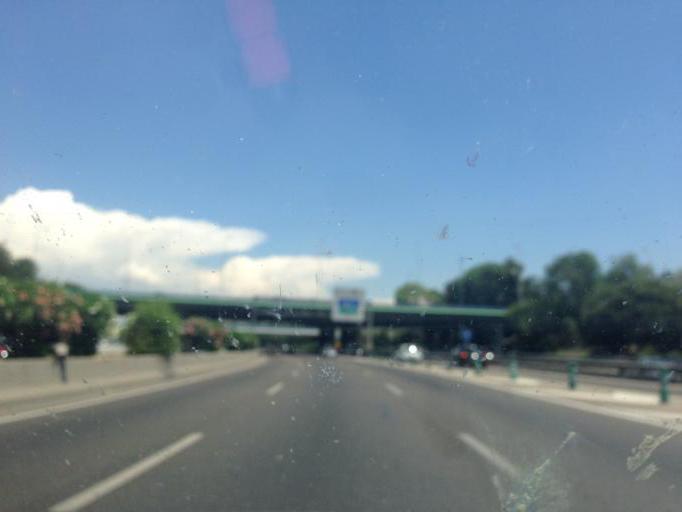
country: ES
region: Madrid
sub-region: Provincia de Madrid
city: Moratalaz
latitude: 40.4174
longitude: -3.6590
